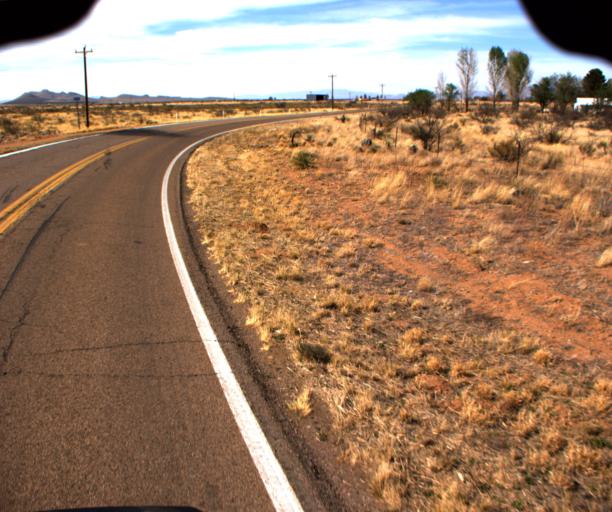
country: US
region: Arizona
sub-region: Cochise County
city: Willcox
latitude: 31.8770
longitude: -109.6608
